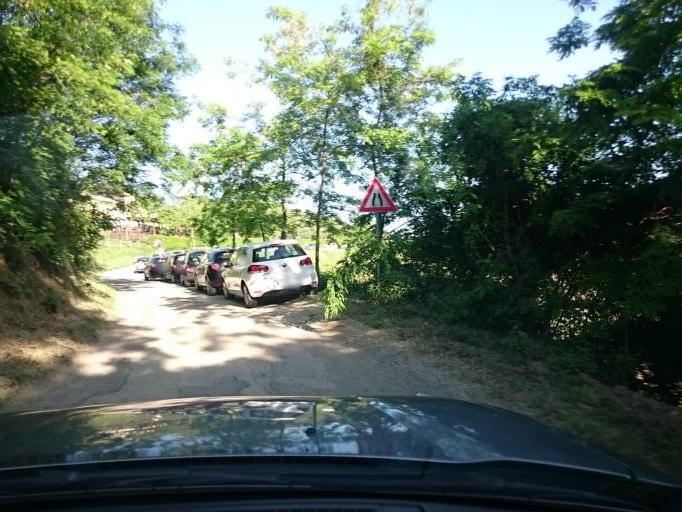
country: IT
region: Veneto
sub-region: Provincia di Padova
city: Galzignano
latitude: 45.2989
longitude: 11.7031
